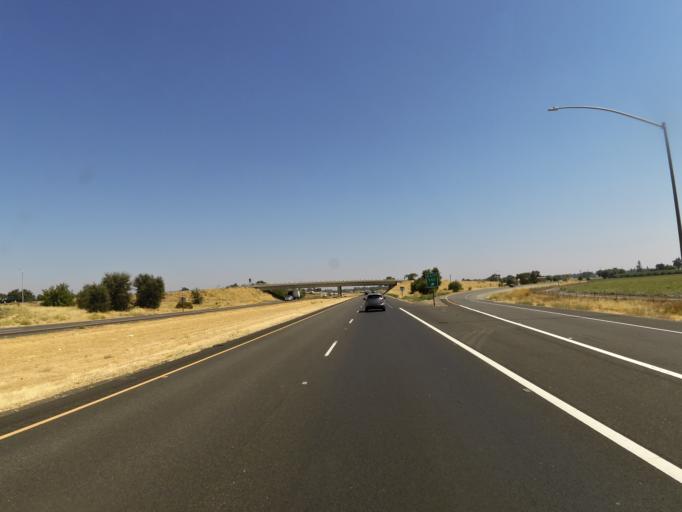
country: US
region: California
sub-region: Yolo County
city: Woodland
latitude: 38.7047
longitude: -121.7859
